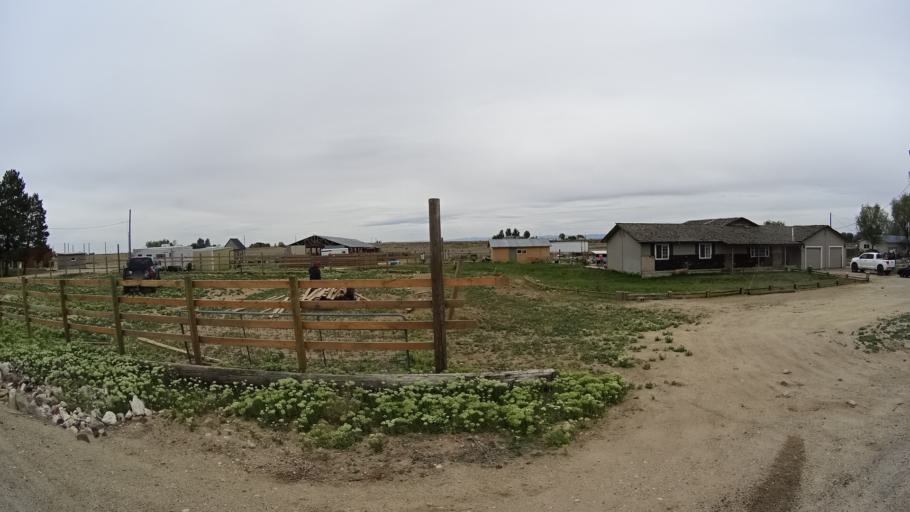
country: US
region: Idaho
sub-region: Ada County
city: Kuna
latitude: 43.4883
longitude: -116.3063
